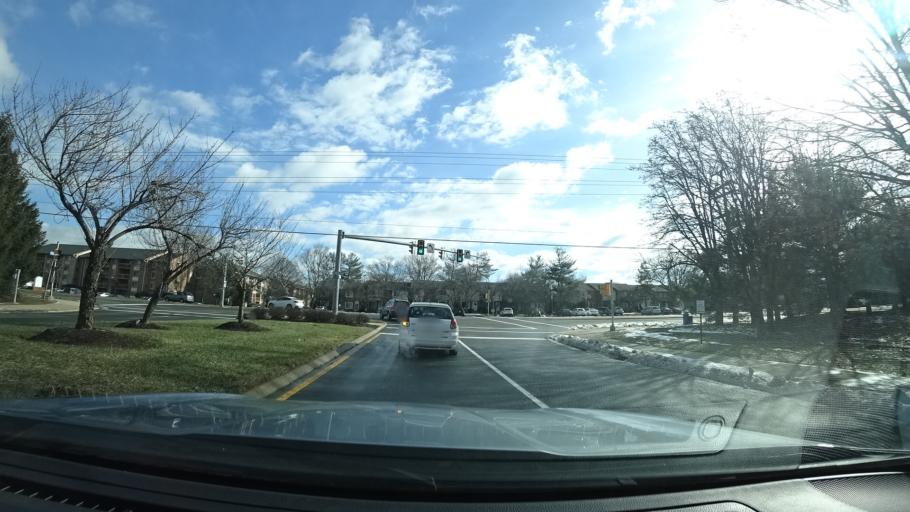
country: US
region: Virginia
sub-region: Loudoun County
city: Sugarland Run
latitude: 39.0357
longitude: -77.3871
